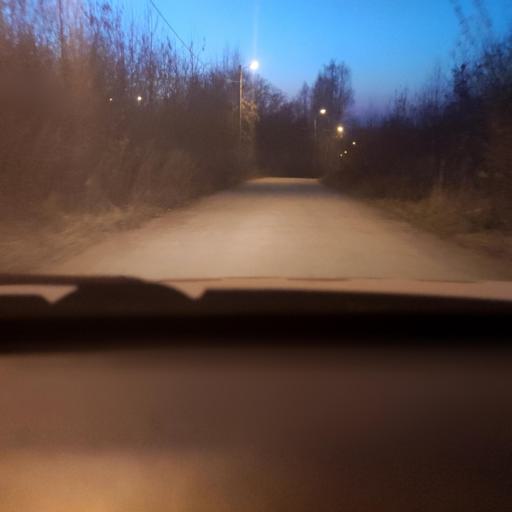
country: RU
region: Perm
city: Perm
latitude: 58.0568
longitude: 56.3407
